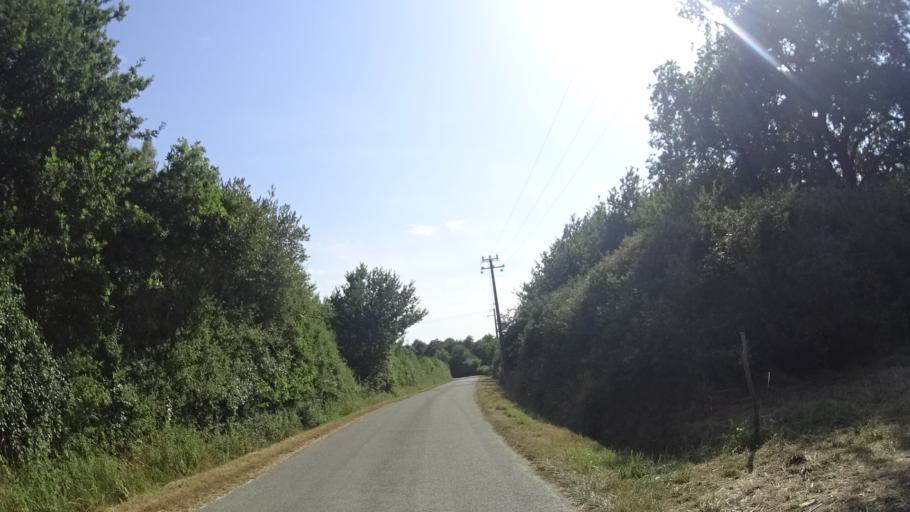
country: FR
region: Pays de la Loire
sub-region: Departement de la Loire-Atlantique
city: Prinquiau
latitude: 47.3320
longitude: -2.0344
